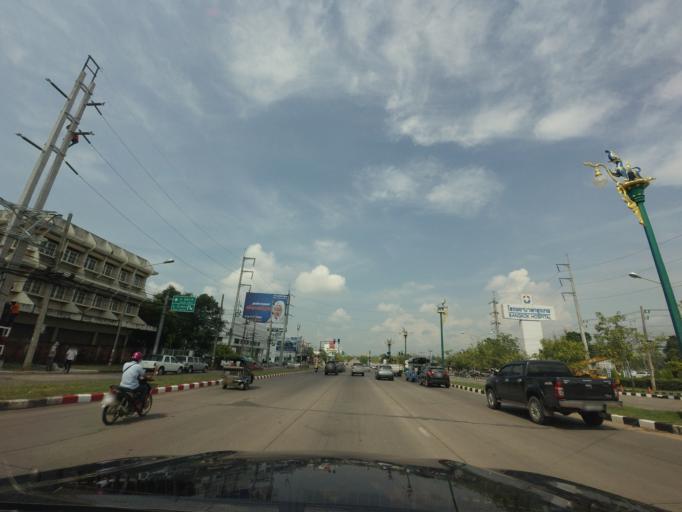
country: TH
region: Khon Kaen
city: Khon Kaen
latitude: 16.4407
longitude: 102.8206
